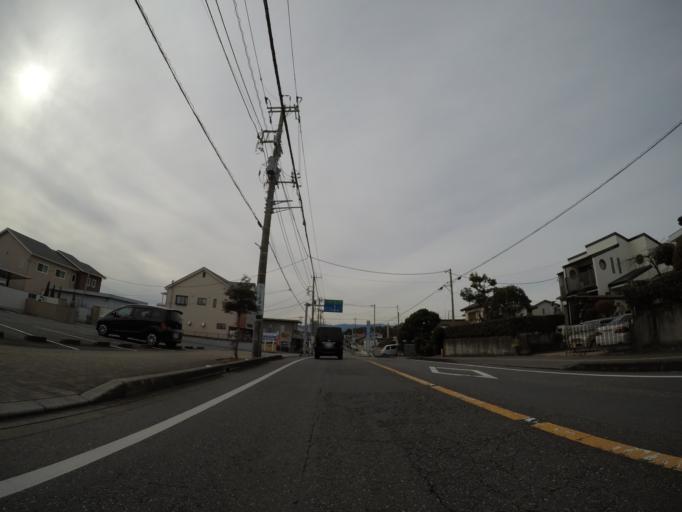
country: JP
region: Shizuoka
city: Fuji
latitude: 35.1849
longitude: 138.6835
